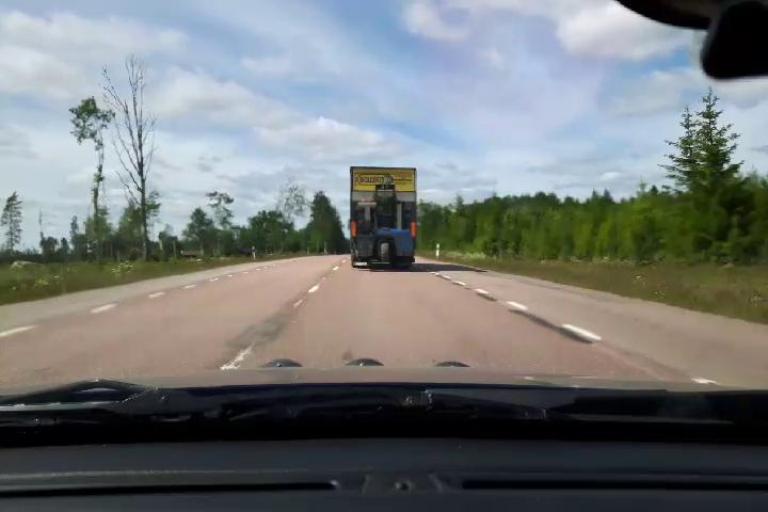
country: SE
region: Uppsala
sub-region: Osthammars Kommun
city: Bjorklinge
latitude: 60.1086
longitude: 17.5395
